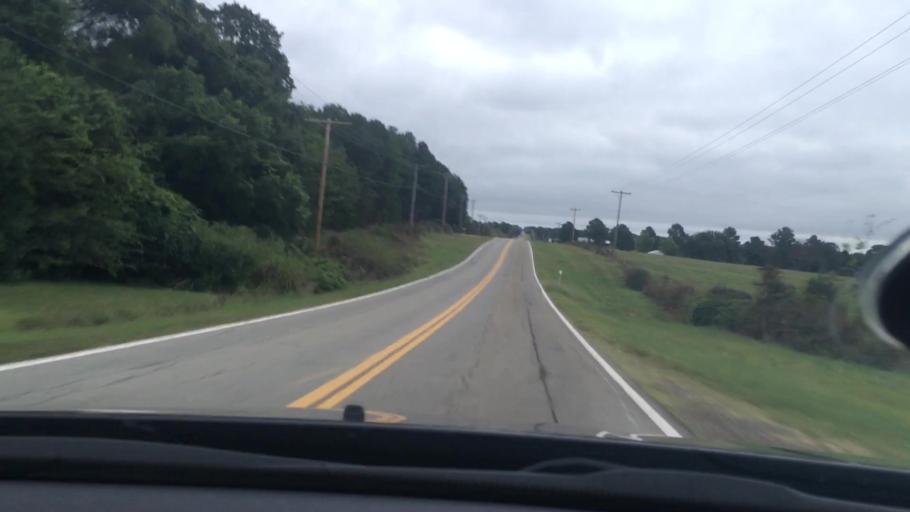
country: US
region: Oklahoma
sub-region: Sequoyah County
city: Vian
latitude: 35.6097
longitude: -94.9852
